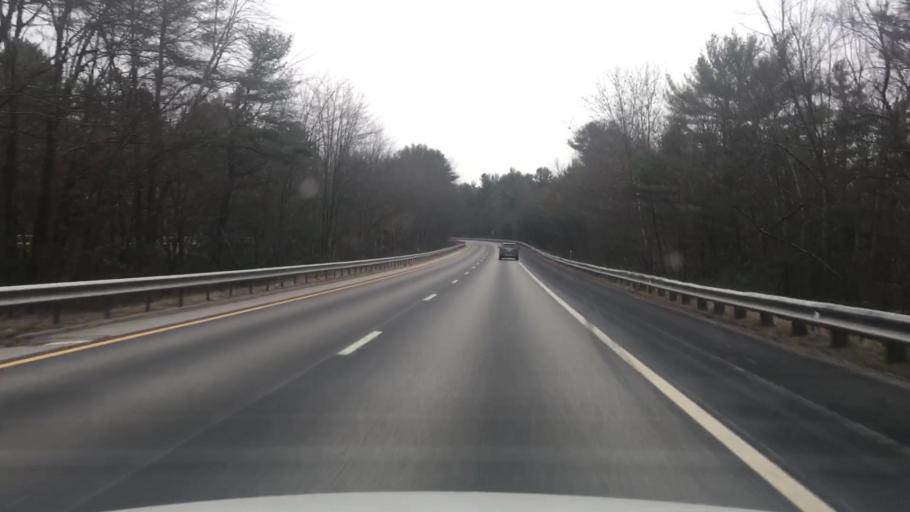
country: US
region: New Hampshire
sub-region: Merrimack County
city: Hopkinton
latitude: 43.1766
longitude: -71.6200
